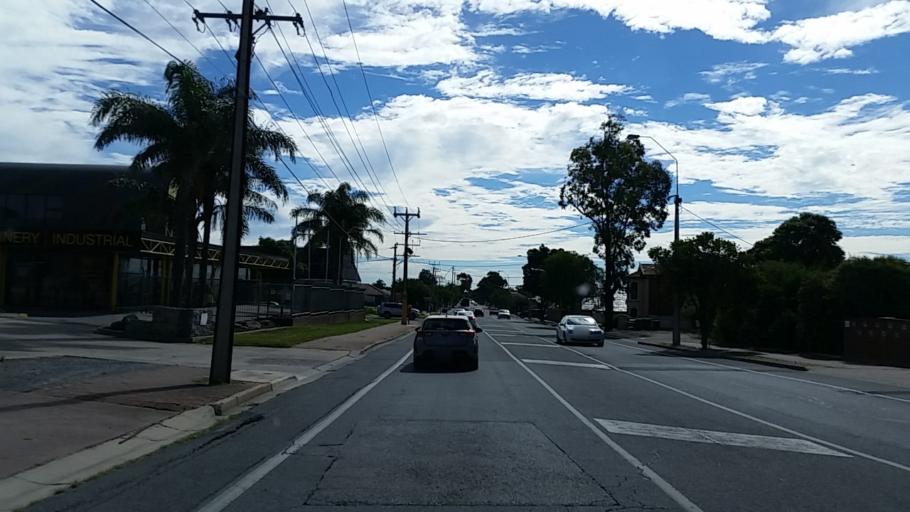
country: AU
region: South Australia
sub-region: Campbelltown
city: Paradise
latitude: -34.8758
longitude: 138.6843
